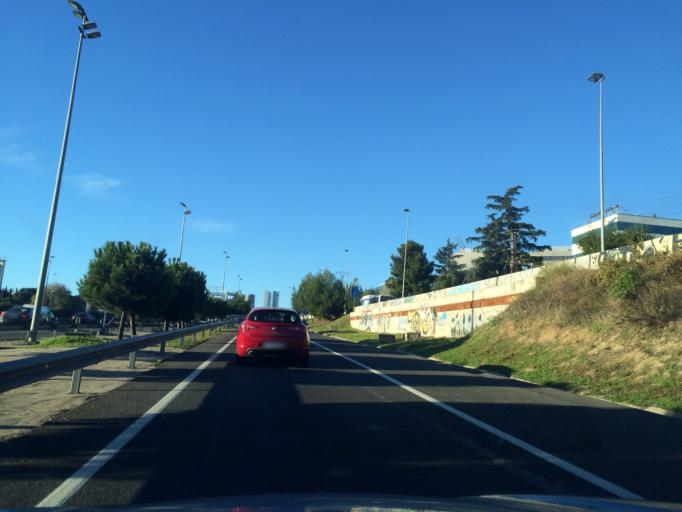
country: ES
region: Madrid
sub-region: Provincia de Madrid
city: Las Tablas
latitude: 40.4942
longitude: -3.6691
